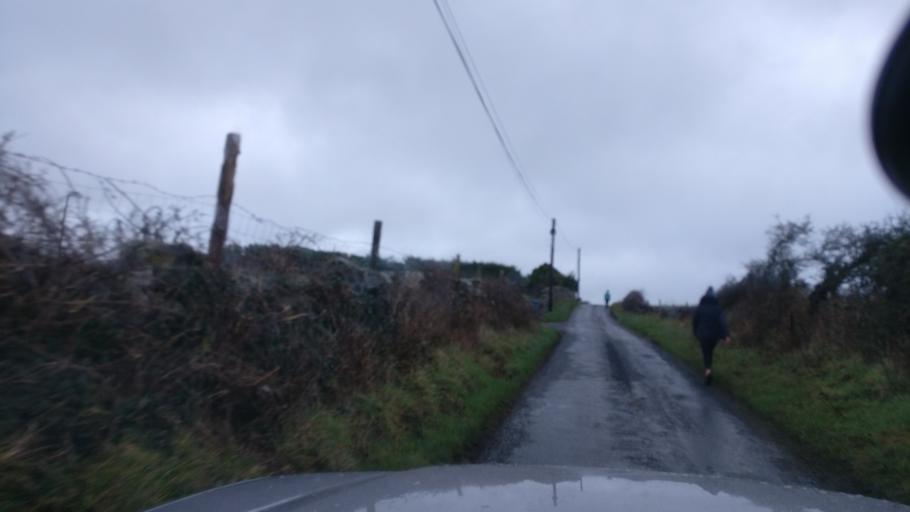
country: IE
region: Connaught
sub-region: County Galway
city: Loughrea
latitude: 53.1935
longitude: -8.6072
